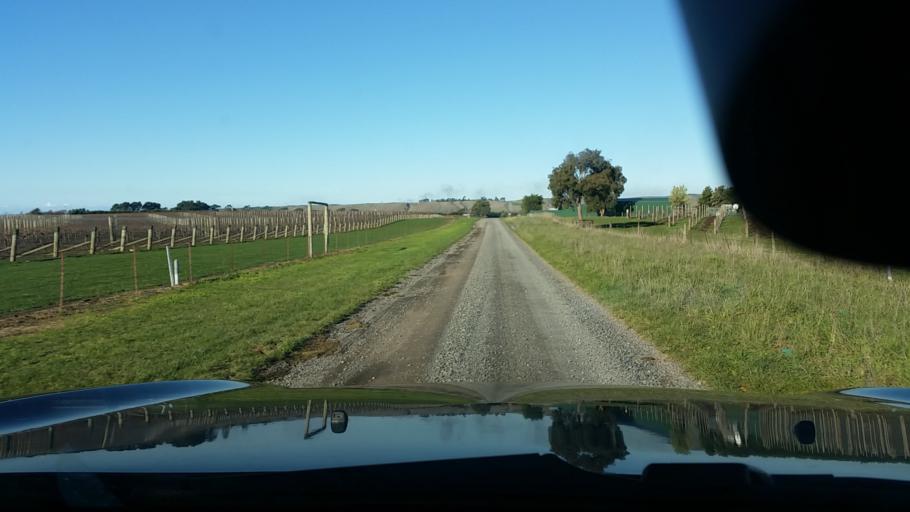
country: NZ
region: Marlborough
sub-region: Marlborough District
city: Blenheim
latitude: -41.6439
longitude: 174.0462
